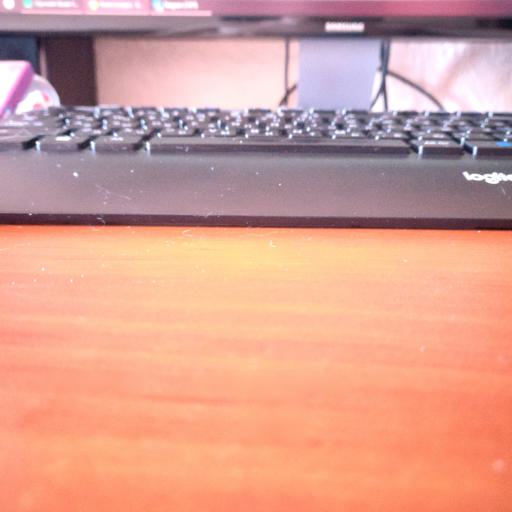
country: FI
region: Haeme
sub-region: Forssa
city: Jokioinen
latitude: 60.7182
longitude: 23.5005
